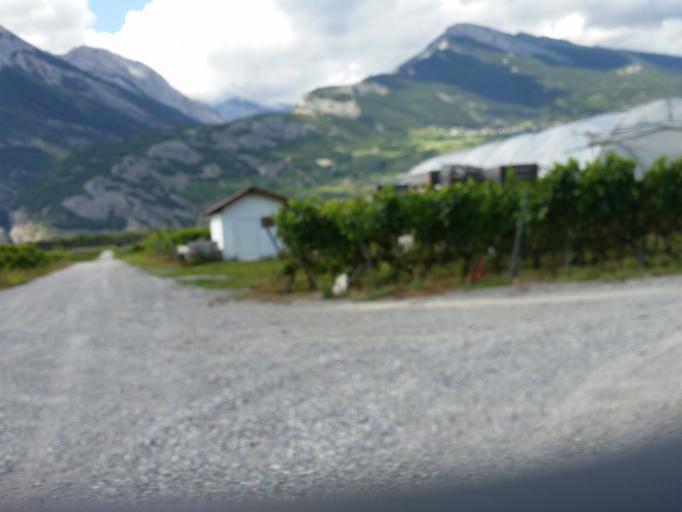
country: CH
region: Valais
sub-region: Conthey District
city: Ardon
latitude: 46.2013
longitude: 7.2775
